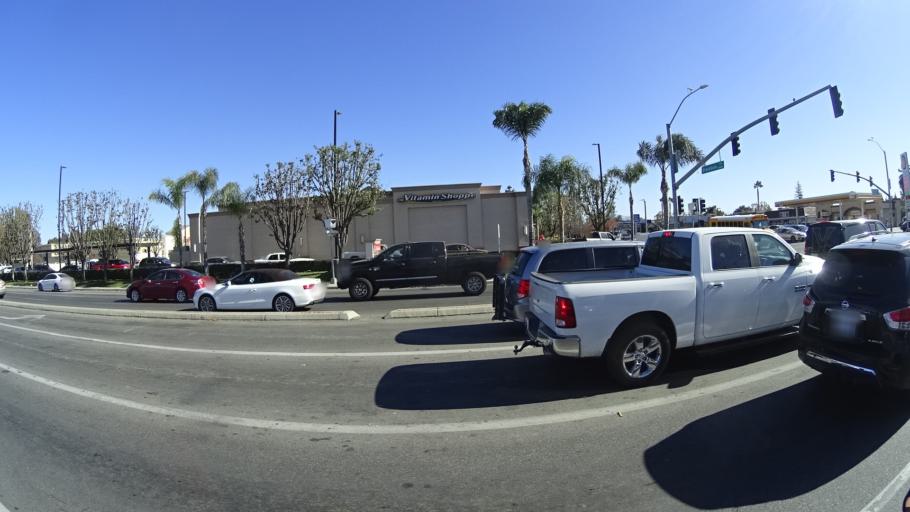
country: US
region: California
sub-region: Kern County
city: Bakersfield
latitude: 35.3547
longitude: -119.0612
